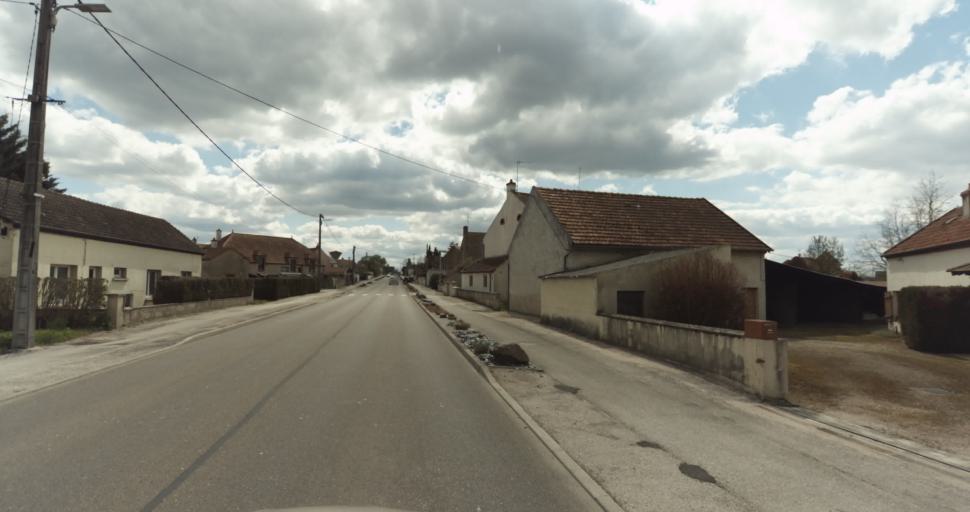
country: FR
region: Bourgogne
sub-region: Departement de la Cote-d'Or
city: Auxonne
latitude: 47.1852
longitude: 5.3991
